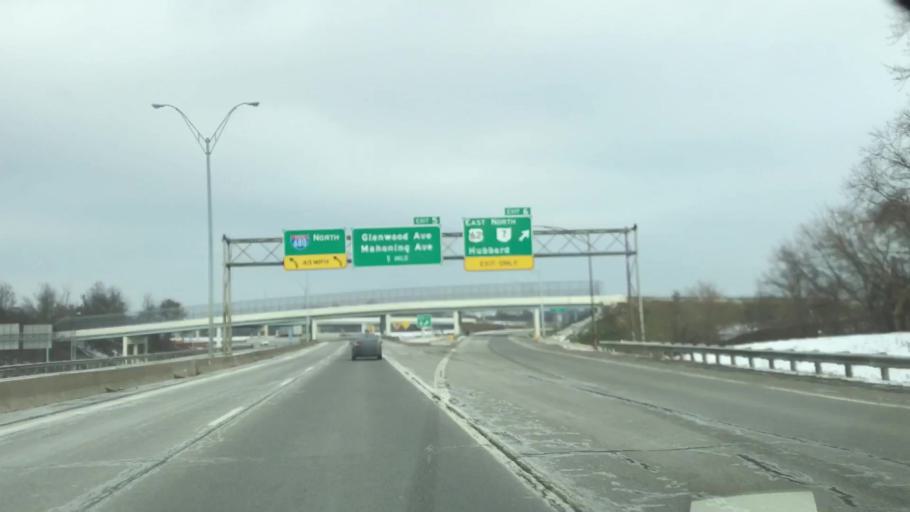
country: US
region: Ohio
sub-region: Mahoning County
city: Youngstown
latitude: 41.0882
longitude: -80.6501
